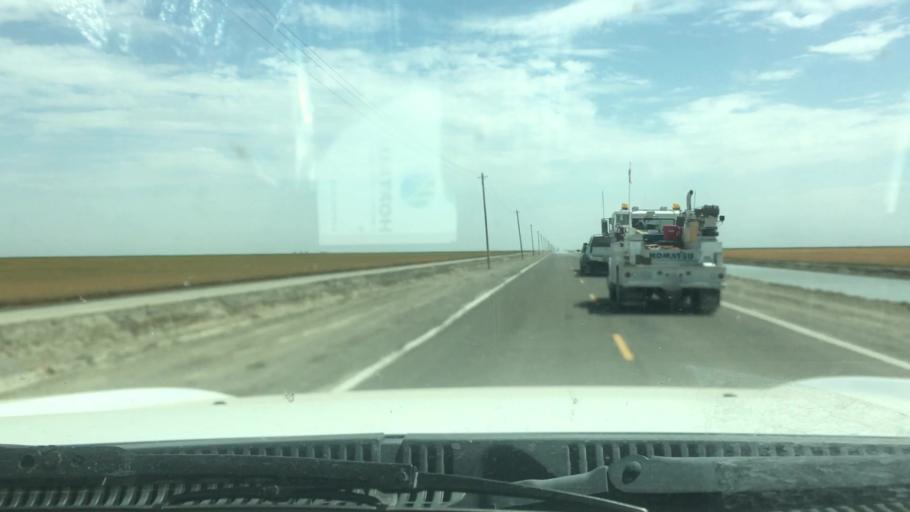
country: US
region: California
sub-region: Tulare County
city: Alpaugh
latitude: 35.9200
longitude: -119.5733
